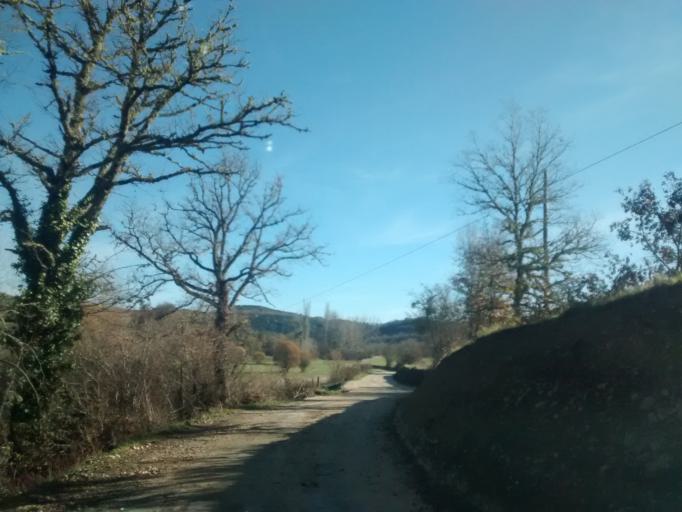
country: ES
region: Cantabria
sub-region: Provincia de Cantabria
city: San Pedro del Romeral
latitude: 42.9646
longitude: -3.7483
